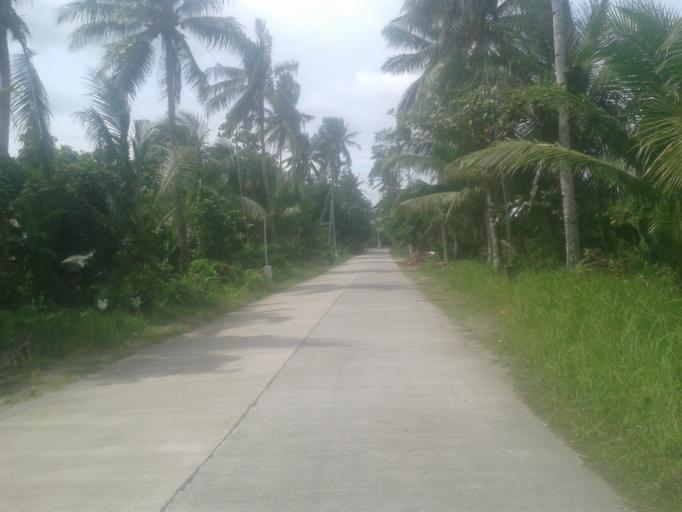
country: PH
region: Eastern Visayas
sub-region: Province of Leyte
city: Mayorga
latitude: 10.8929
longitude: 125.0043
